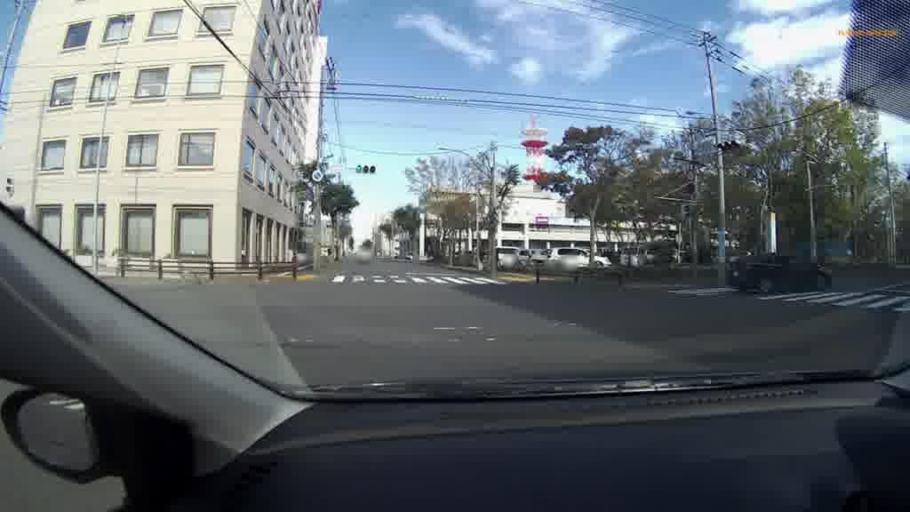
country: JP
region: Hokkaido
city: Kushiro
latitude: 42.9838
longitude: 144.3812
